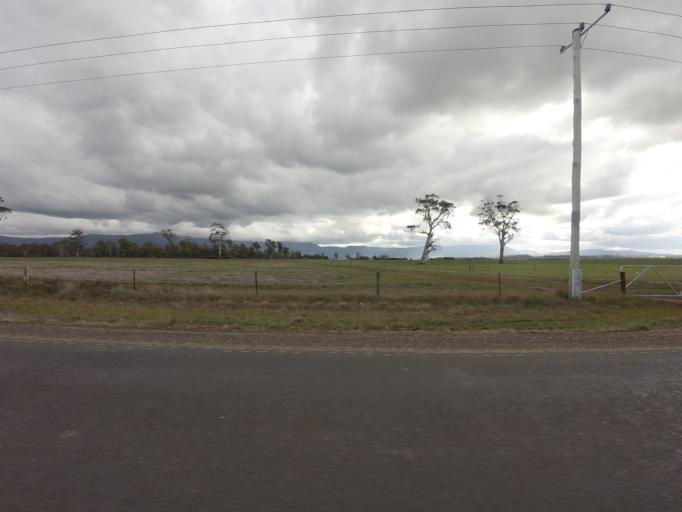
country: AU
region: Tasmania
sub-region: Northern Midlands
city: Longford
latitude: -41.7632
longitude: 147.0835
